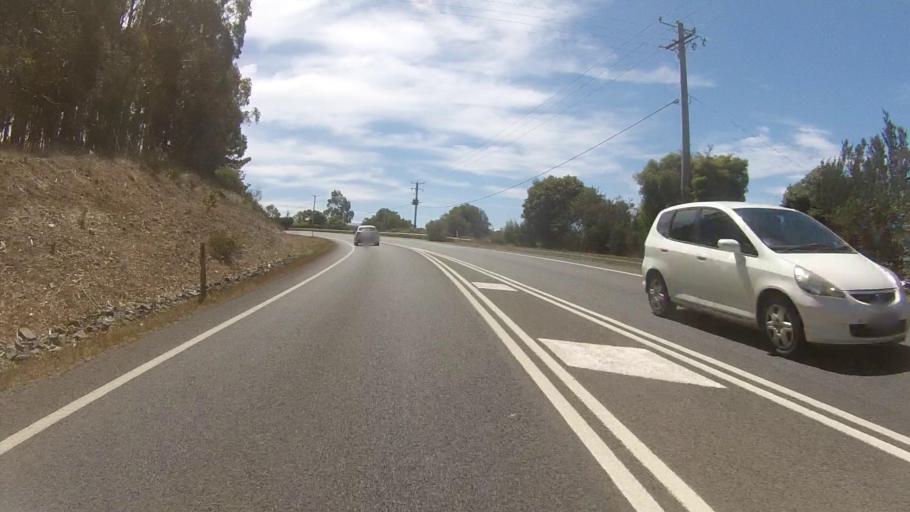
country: AU
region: Tasmania
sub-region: Kingborough
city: Margate
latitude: -43.0042
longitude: 147.2751
